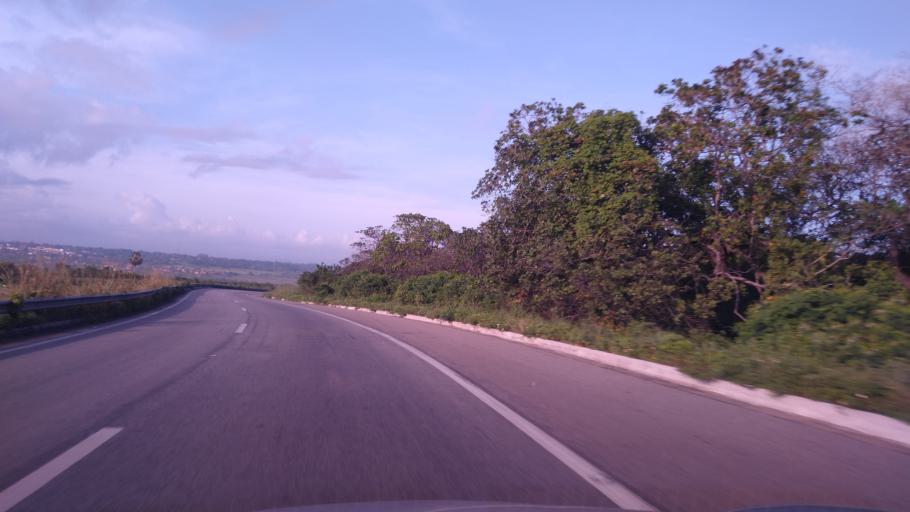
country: BR
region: Ceara
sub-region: Pacajus
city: Pacajus
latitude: -4.1487
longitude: -38.4785
